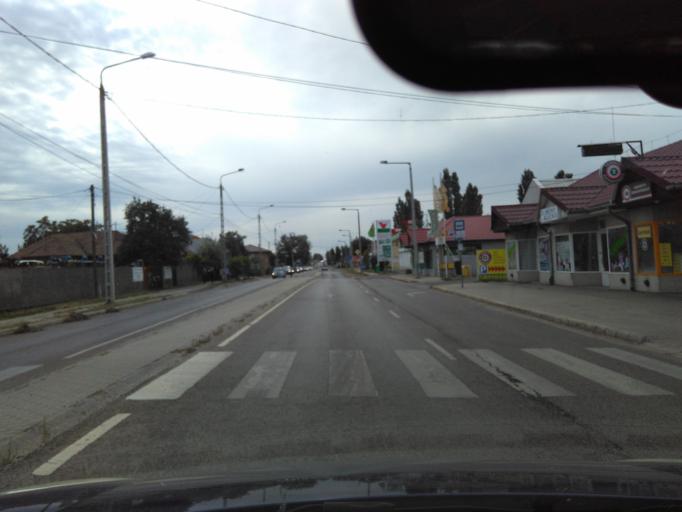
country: HU
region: Pest
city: Kistarcsa
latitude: 47.5515
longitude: 19.2692
